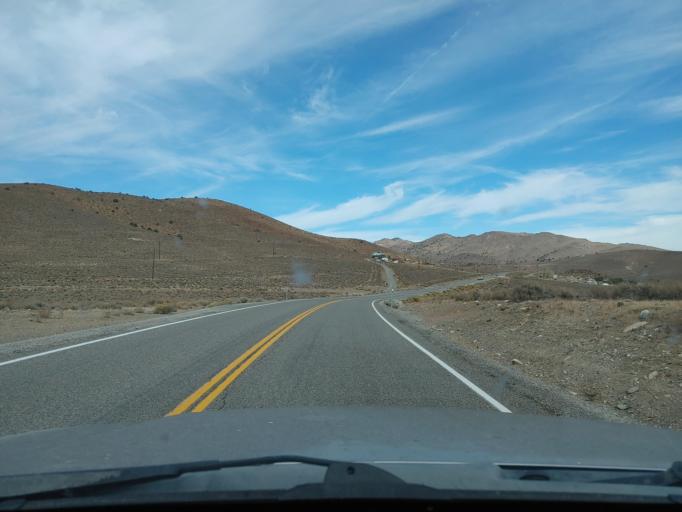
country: US
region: Nevada
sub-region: Lyon County
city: Dayton
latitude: 39.2313
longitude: -119.6459
